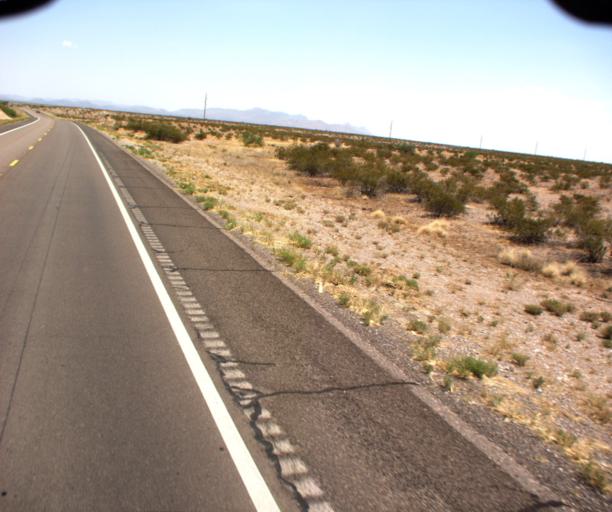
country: US
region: Arizona
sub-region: Graham County
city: Safford
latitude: 32.8041
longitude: -109.5783
